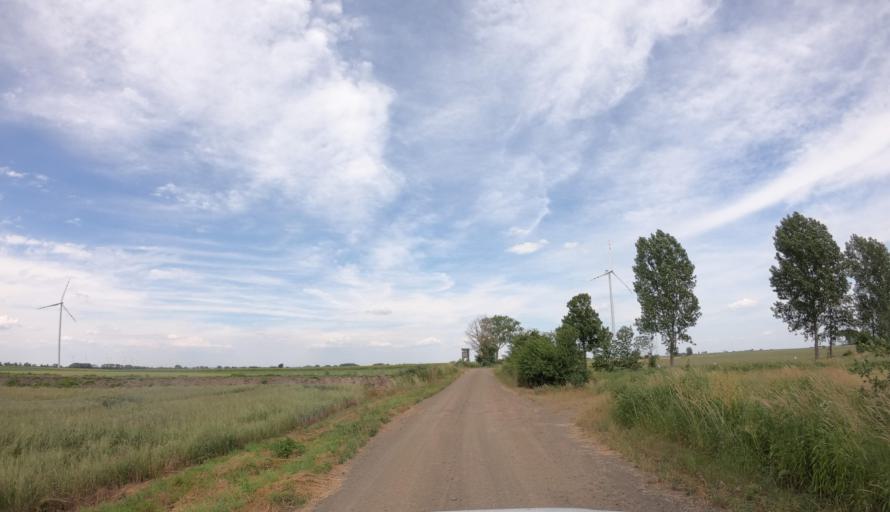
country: PL
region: West Pomeranian Voivodeship
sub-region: Powiat pyrzycki
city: Kozielice
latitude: 53.1116
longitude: 14.8243
